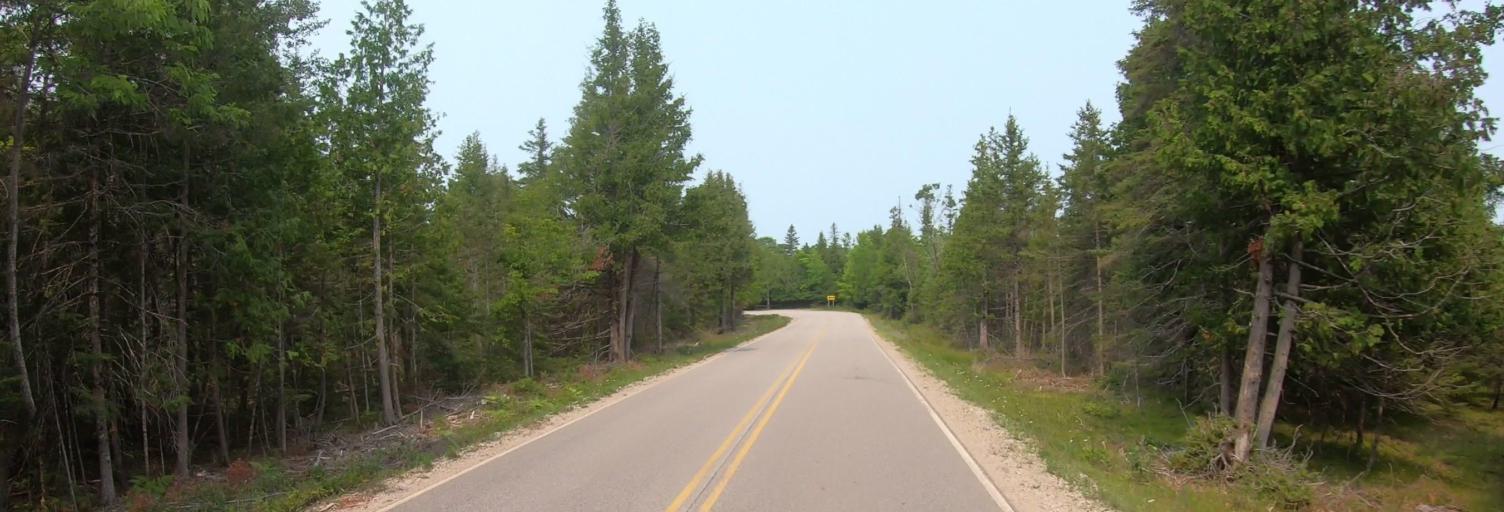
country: CA
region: Ontario
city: Thessalon
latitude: 46.0152
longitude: -83.7076
